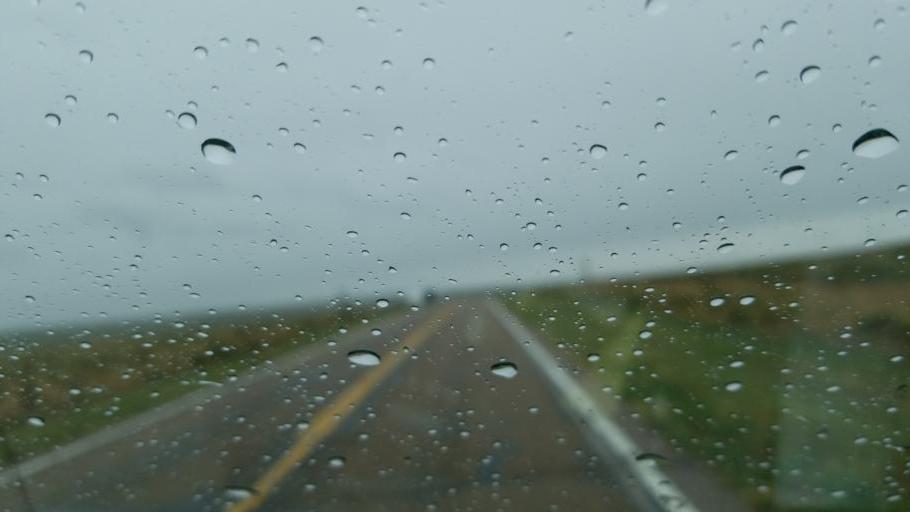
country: US
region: Colorado
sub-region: Lincoln County
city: Hugo
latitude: 38.8505
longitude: -103.1610
